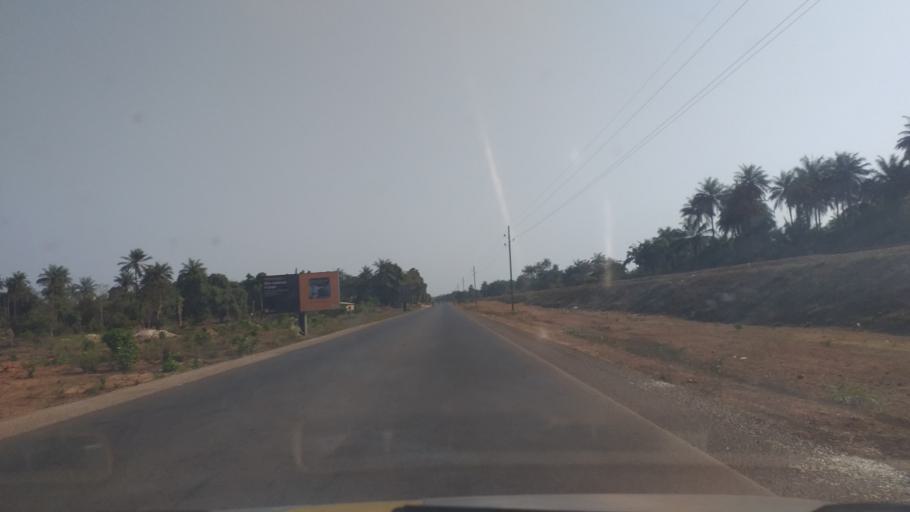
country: GN
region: Boke
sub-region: Boke Prefecture
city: Kamsar
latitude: 10.7498
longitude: -14.5084
